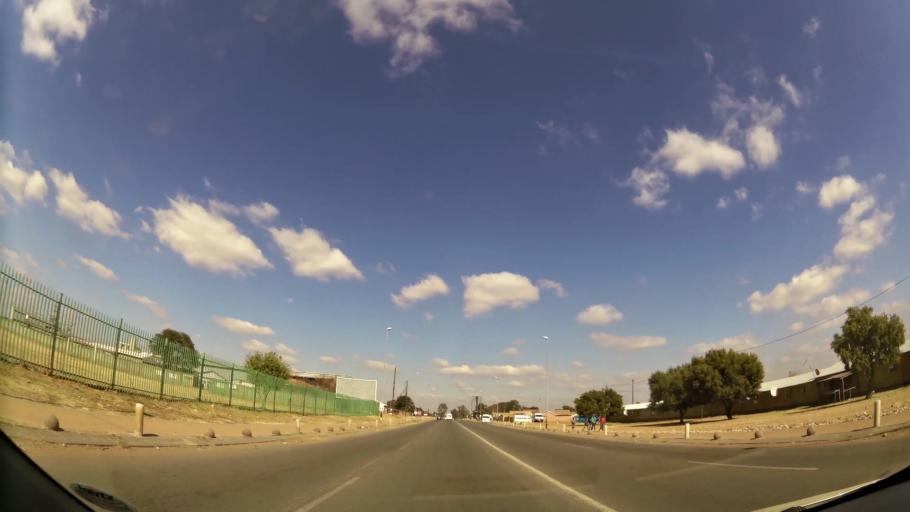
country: ZA
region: Gauteng
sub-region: West Rand District Municipality
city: Krugersdorp
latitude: -26.1421
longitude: 27.7931
